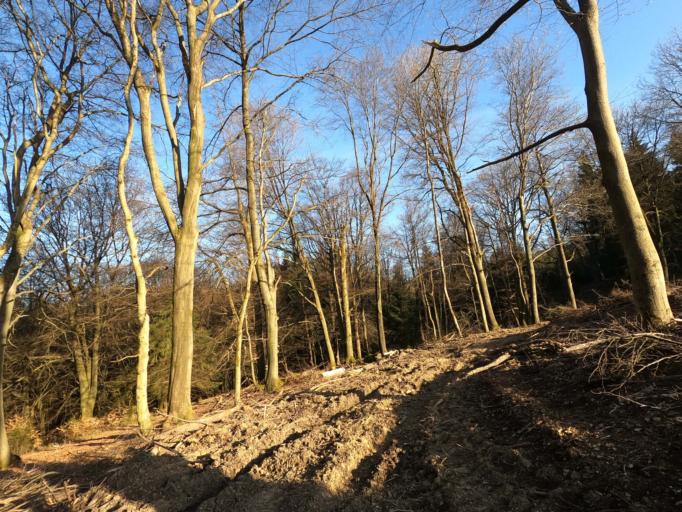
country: DE
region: North Rhine-Westphalia
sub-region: Regierungsbezirk Arnsberg
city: Herscheid
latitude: 51.1650
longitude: 7.7310
